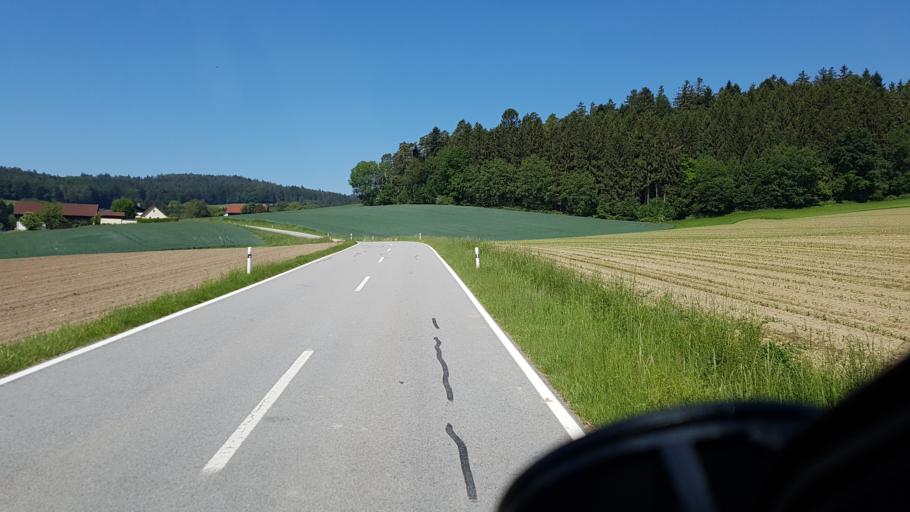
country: DE
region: Bavaria
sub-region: Lower Bavaria
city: Stubenberg
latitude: 48.2939
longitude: 13.0638
